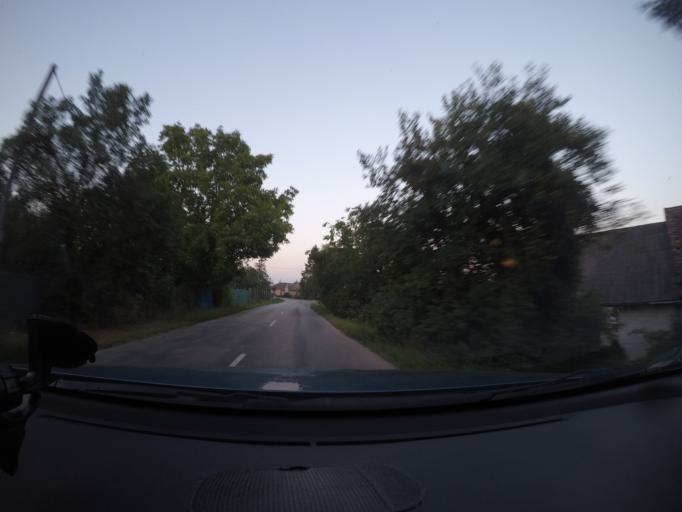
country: SK
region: Trenciansky
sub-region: Okres Trencin
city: Trencin
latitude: 48.8509
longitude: 17.9246
